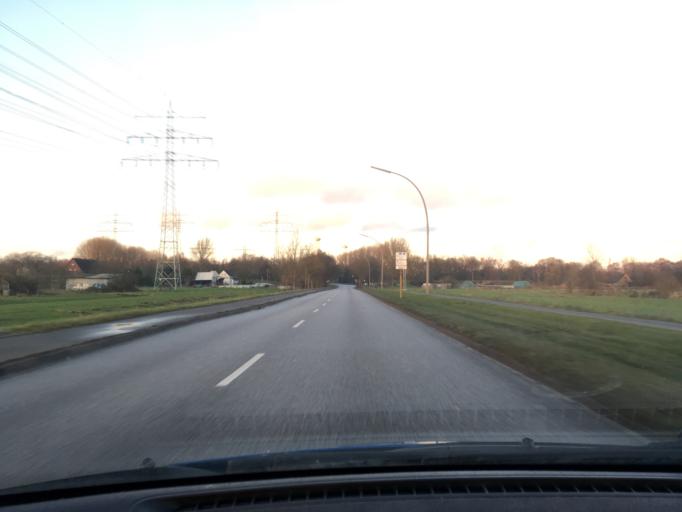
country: DE
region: Hamburg
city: Altona
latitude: 53.4924
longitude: 9.9084
